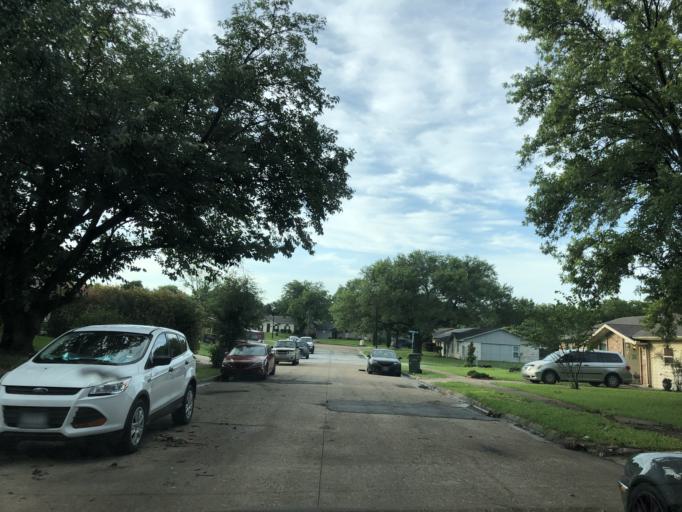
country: US
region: Texas
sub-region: Dallas County
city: Sunnyvale
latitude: 32.8484
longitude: -96.6010
